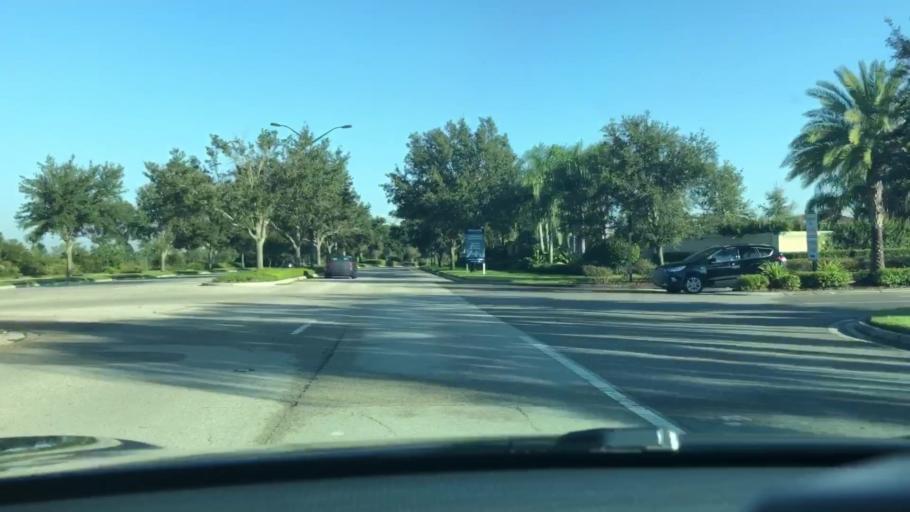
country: US
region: Florida
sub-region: Orange County
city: Meadow Woods
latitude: 28.3896
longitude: -81.2760
